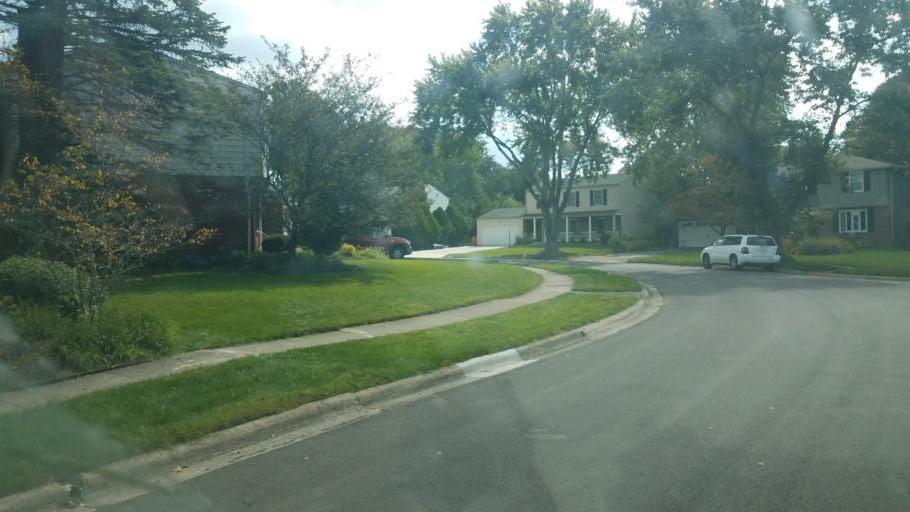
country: US
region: Ohio
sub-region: Franklin County
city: Worthington
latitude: 40.1032
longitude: -83.0245
